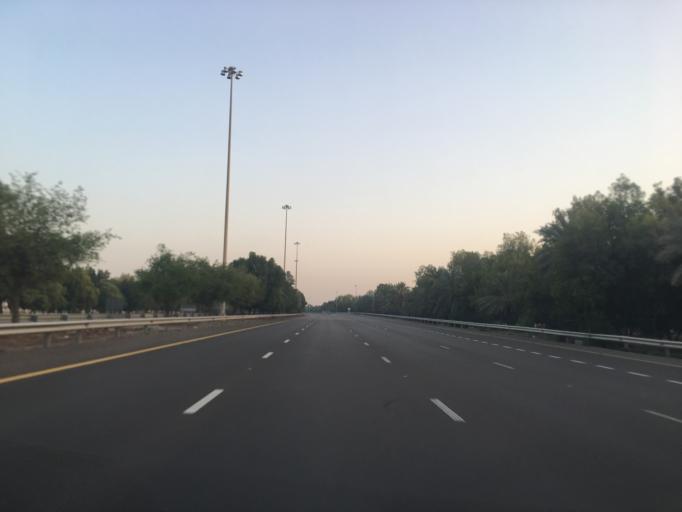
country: AE
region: Abu Dhabi
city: Abu Dhabi
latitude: 24.3586
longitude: 54.5660
